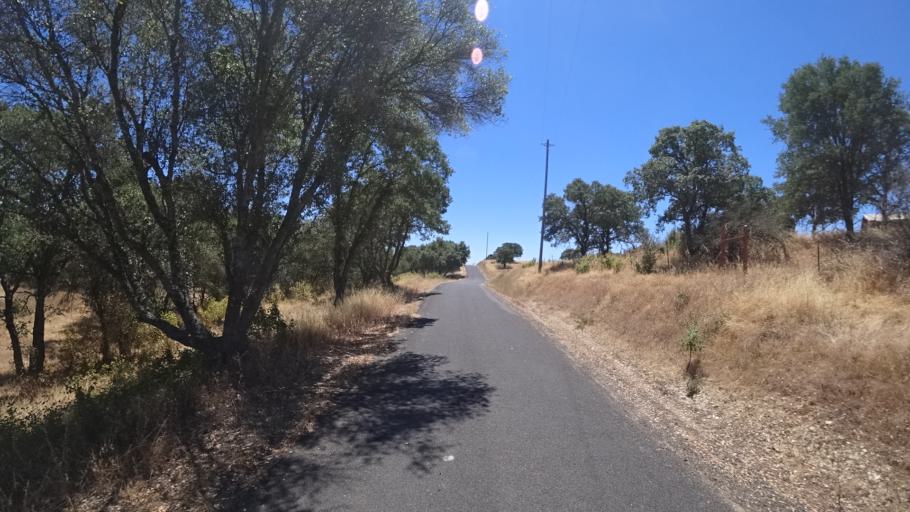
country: US
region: California
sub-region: Calaveras County
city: Copperopolis
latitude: 37.9789
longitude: -120.6899
